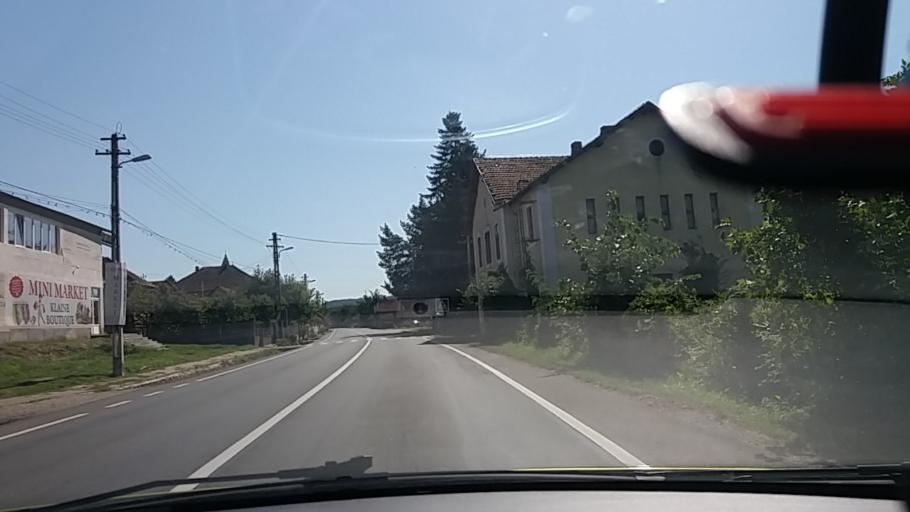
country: RO
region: Arad
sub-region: Comuna Conop
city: Conop
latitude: 46.1022
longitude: 21.8737
